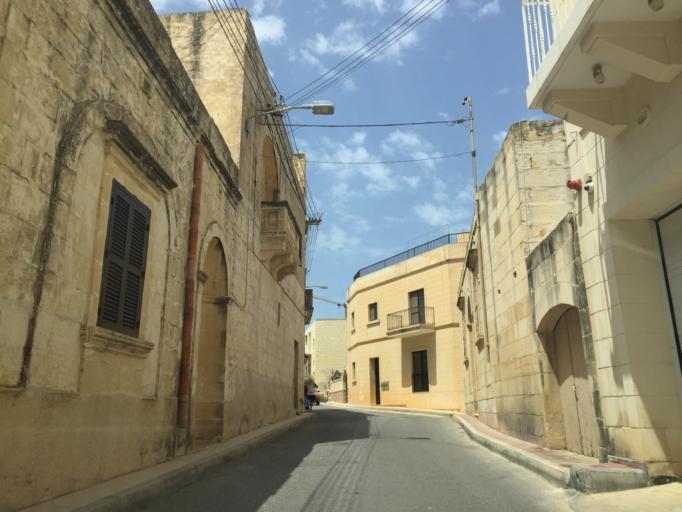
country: MT
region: Ix-Xaghra
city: Xaghra
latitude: 36.0485
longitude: 14.2592
